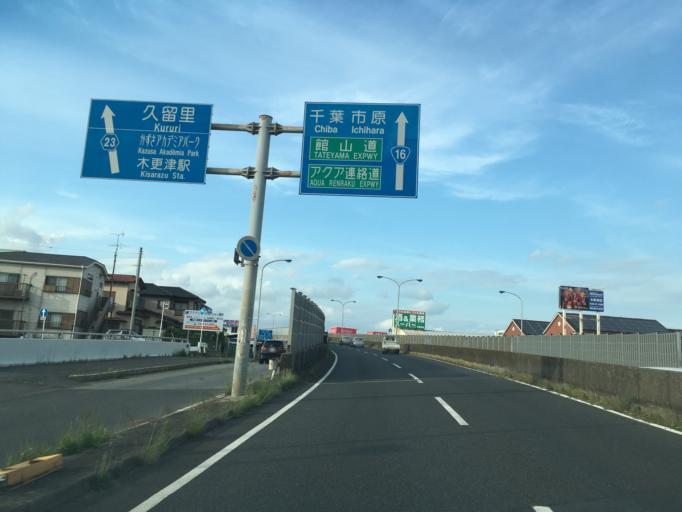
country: JP
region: Chiba
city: Kisarazu
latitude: 35.3758
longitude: 139.9406
